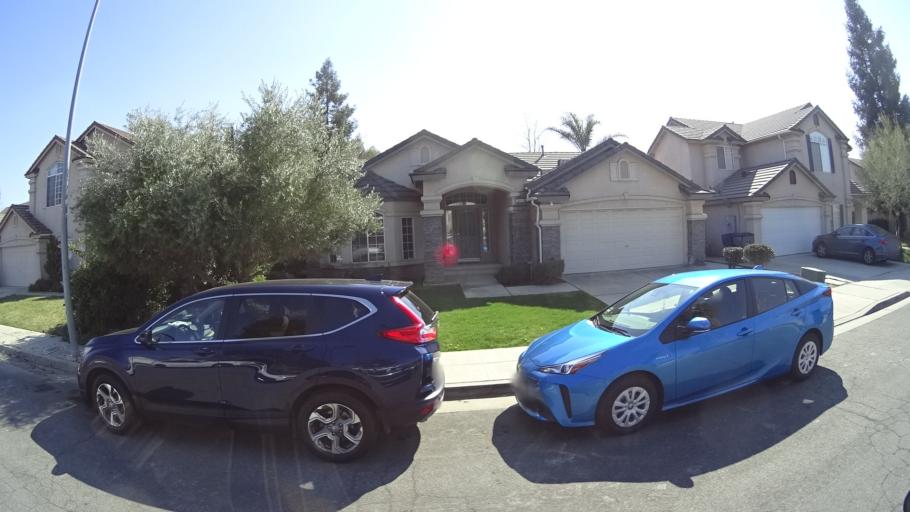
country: US
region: California
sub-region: Fresno County
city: Clovis
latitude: 36.8708
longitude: -119.7326
